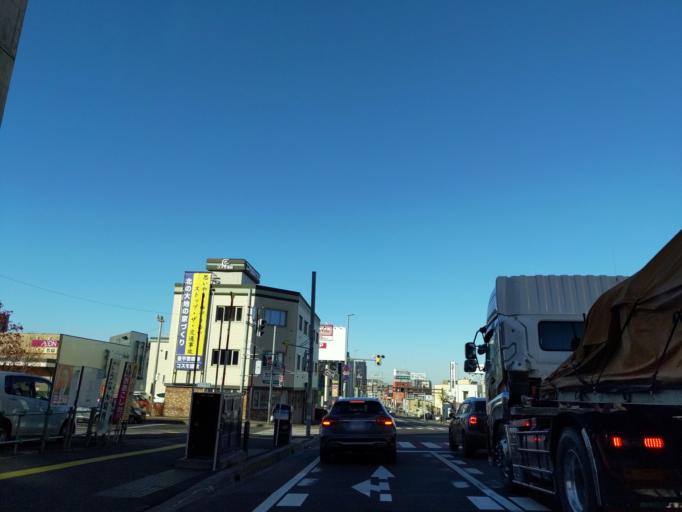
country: JP
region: Hokkaido
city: Sapporo
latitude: 43.0357
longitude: 141.3929
